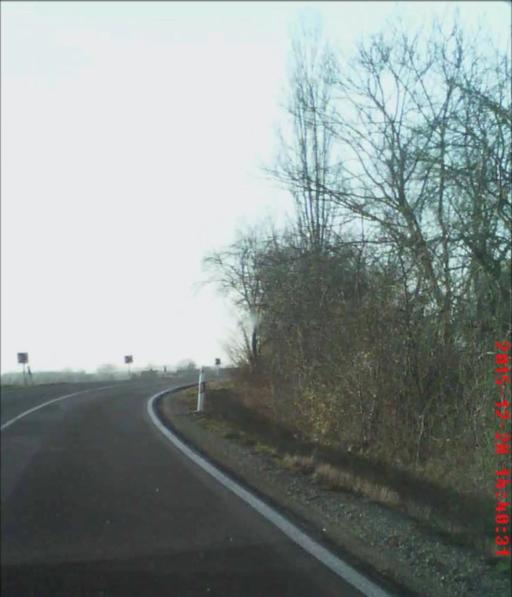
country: DE
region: Thuringia
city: Krautheim
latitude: 51.0714
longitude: 11.3107
